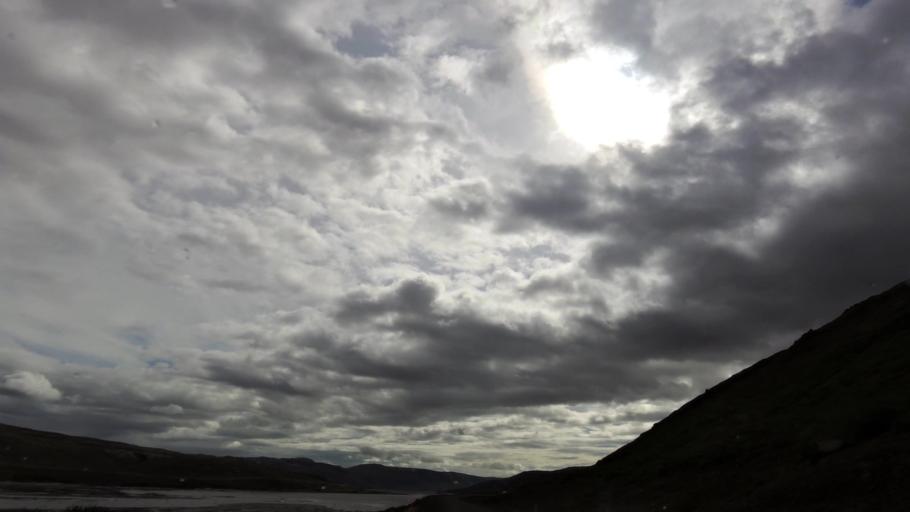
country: IS
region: West
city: Stykkisholmur
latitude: 65.6009
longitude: -22.1124
